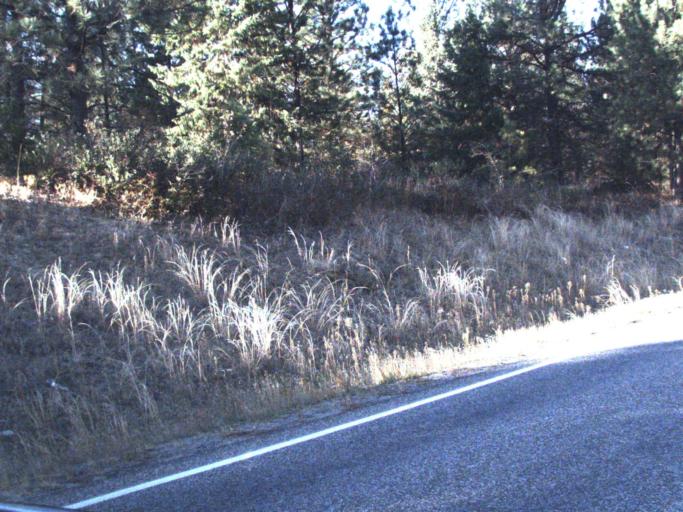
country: CA
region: British Columbia
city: Rossland
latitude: 48.9075
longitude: -117.7924
